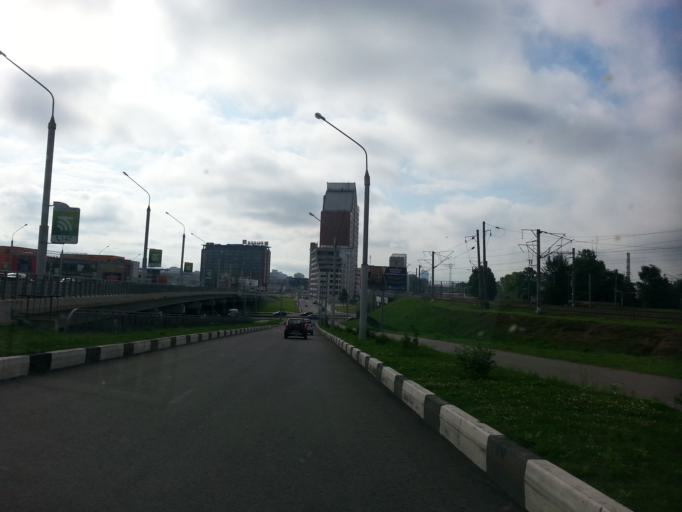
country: BY
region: Minsk
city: Minsk
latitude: 53.9276
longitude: 27.5038
